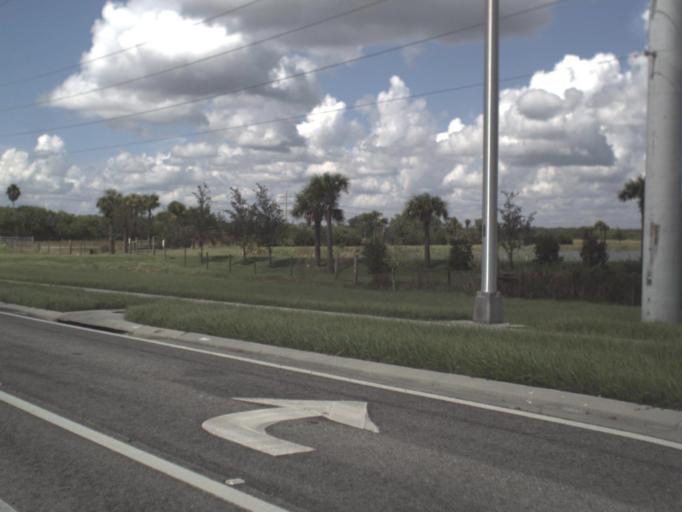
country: US
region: Florida
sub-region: Lee County
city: Tice
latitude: 26.6283
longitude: -81.7810
